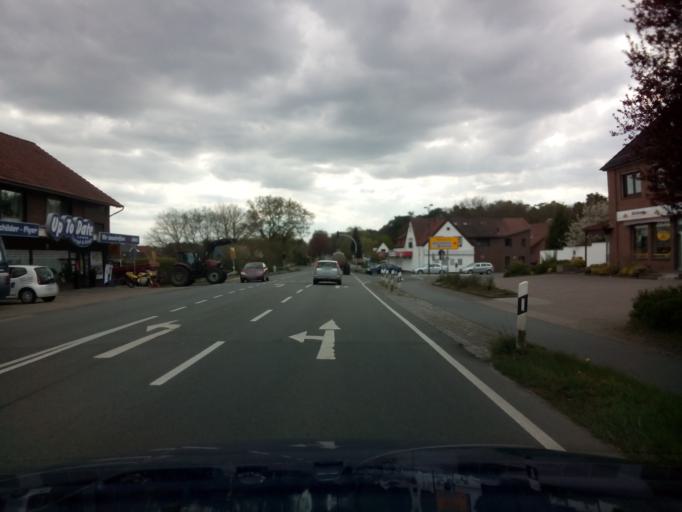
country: DE
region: Lower Saxony
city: Hambergen
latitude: 53.2873
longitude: 8.8278
